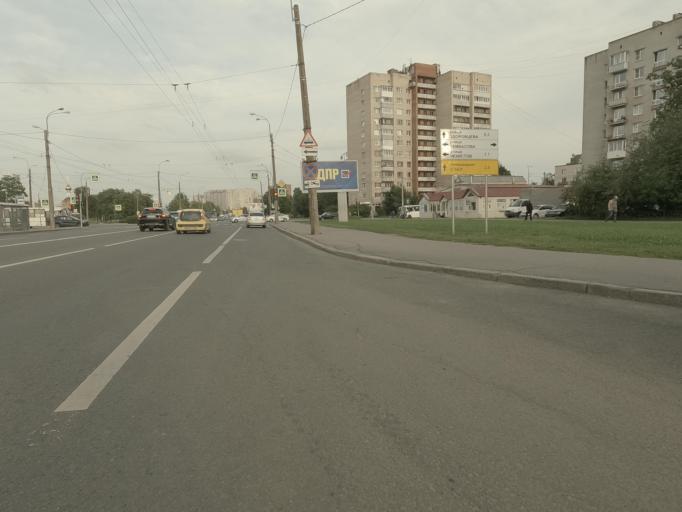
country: RU
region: St.-Petersburg
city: Sosnovaya Polyana
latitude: 59.8347
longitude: 30.1551
